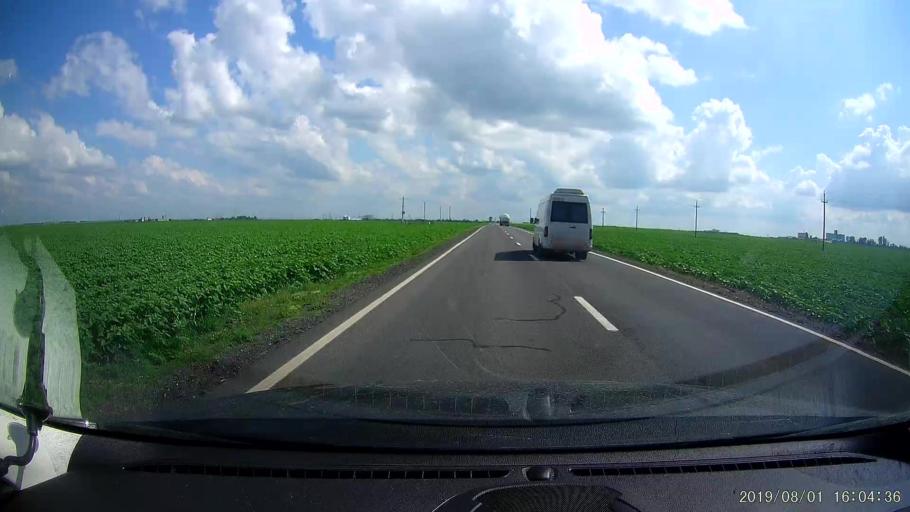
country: RO
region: Calarasi
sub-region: Comuna Dragalina
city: Drajna Noua
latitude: 44.4433
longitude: 27.3794
